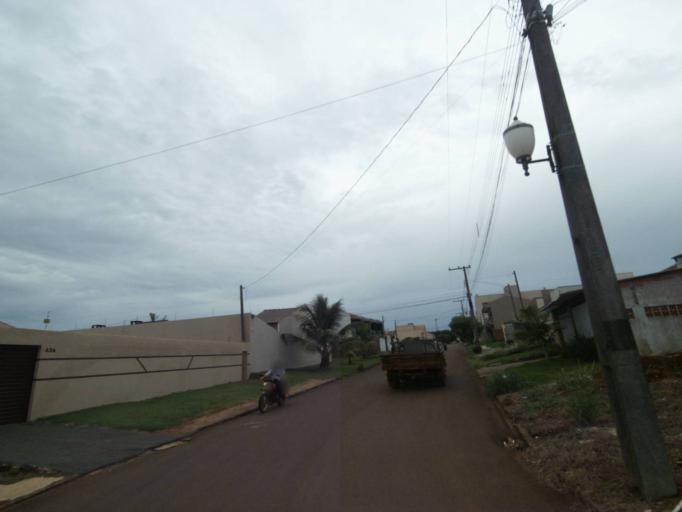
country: BR
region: Parana
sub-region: Campo Mourao
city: Campo Mourao
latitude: -24.0312
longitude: -52.3582
